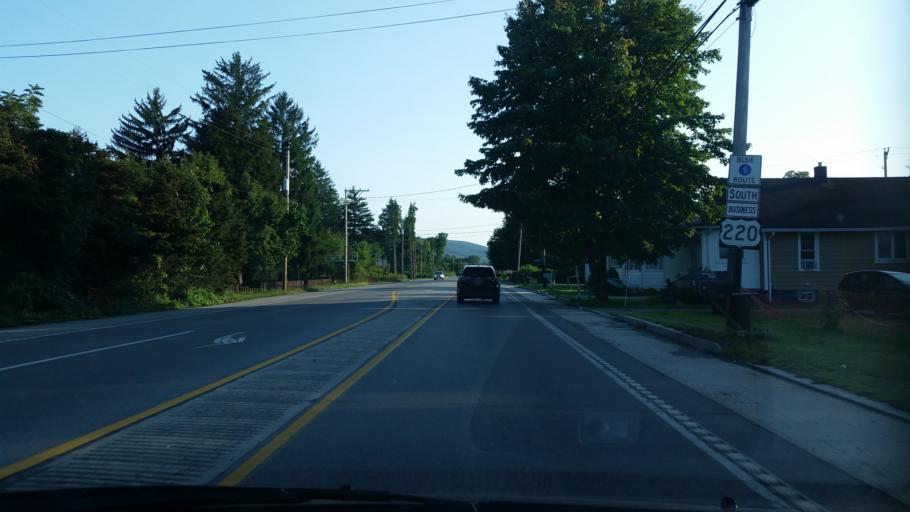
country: US
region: Pennsylvania
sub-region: Blair County
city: Bellwood
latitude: 40.5994
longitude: -78.3206
